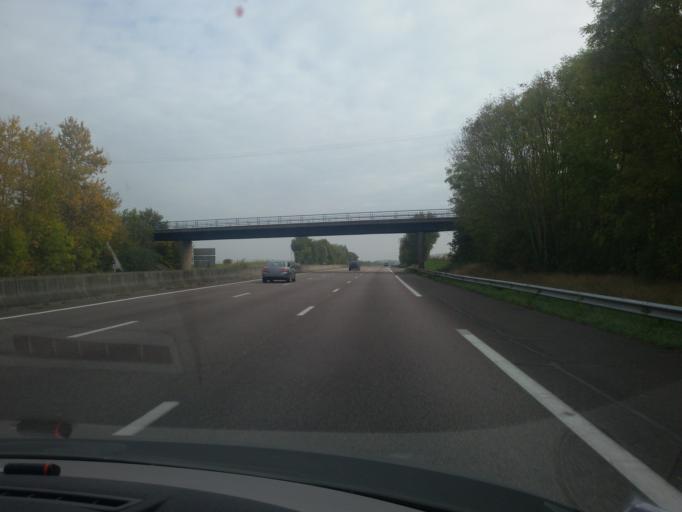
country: FR
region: Haute-Normandie
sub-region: Departement de l'Eure
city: La Chapelle-Reanville
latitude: 49.0738
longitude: 1.4007
